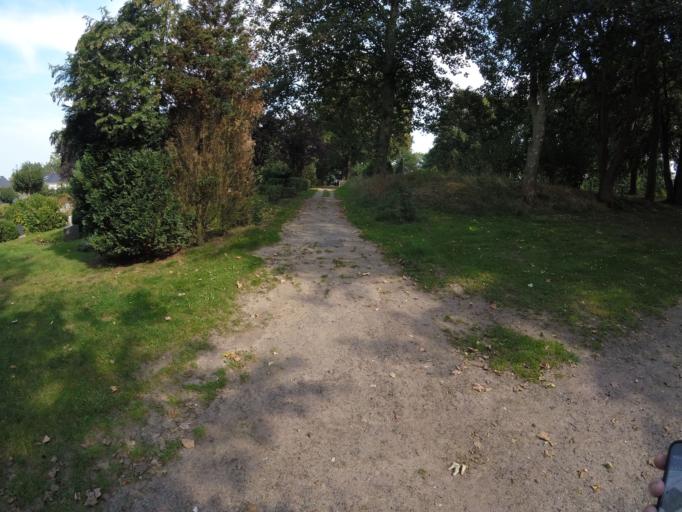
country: DE
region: Lower Saxony
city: Stade
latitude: 53.6110
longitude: 9.4574
